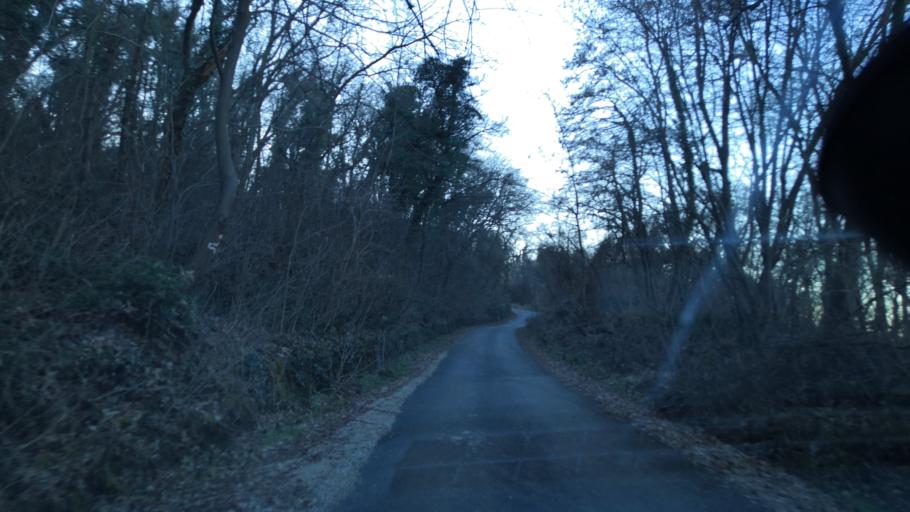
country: RS
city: Cortanovci
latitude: 45.1668
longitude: 20.0038
